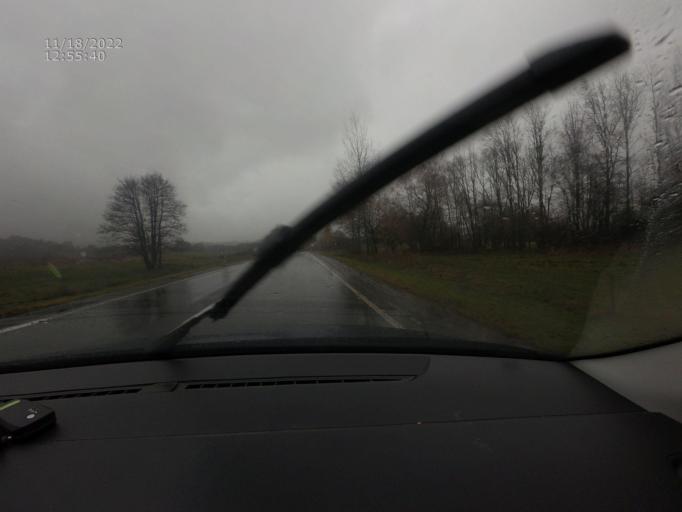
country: CZ
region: Plzensky
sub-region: Okres Klatovy
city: Kolinec
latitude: 49.3359
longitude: 13.4339
